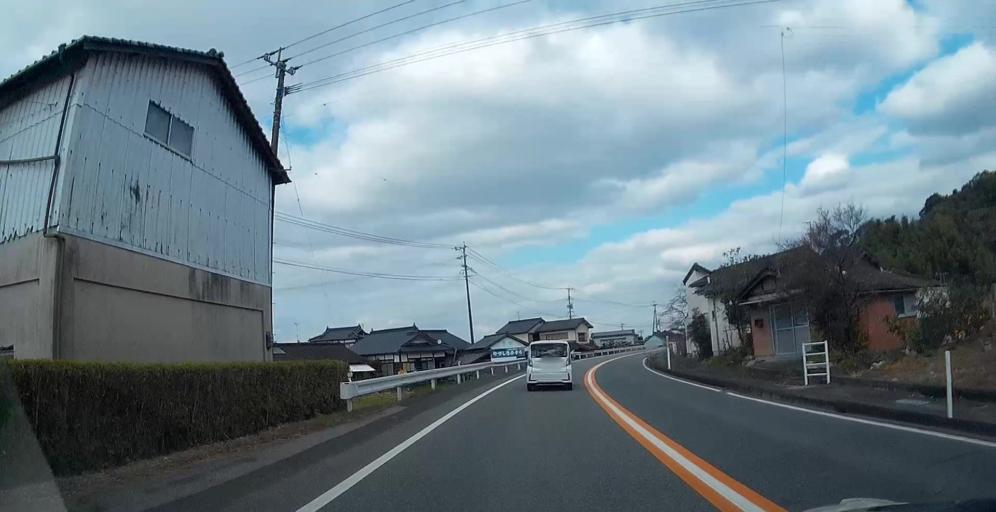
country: JP
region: Kumamoto
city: Yatsushiro
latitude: 32.4464
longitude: 130.5870
